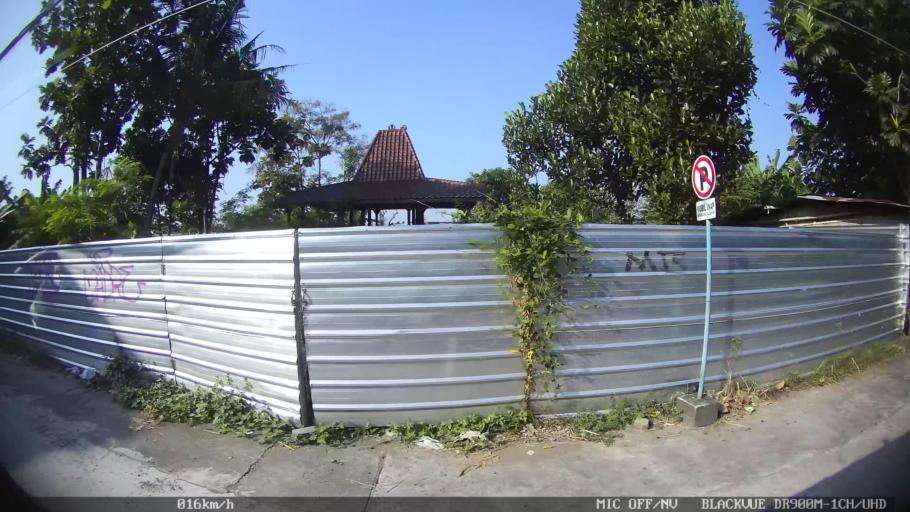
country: ID
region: Daerah Istimewa Yogyakarta
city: Depok
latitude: -7.7741
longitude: 110.4071
